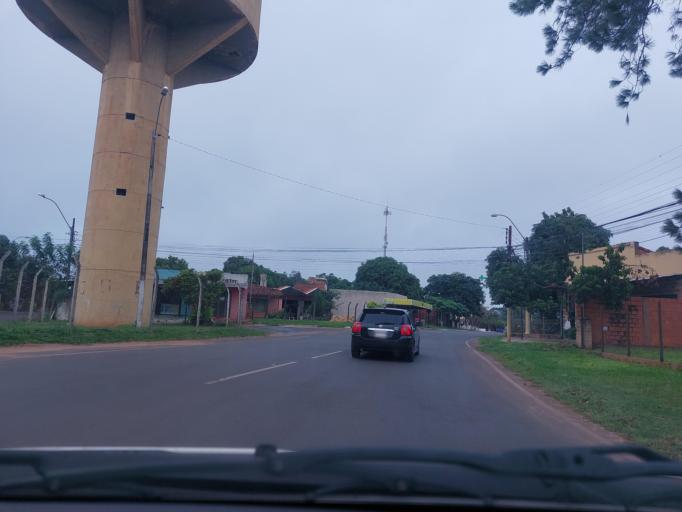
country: PY
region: San Pedro
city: Guayaybi
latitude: -24.6725
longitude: -56.4421
